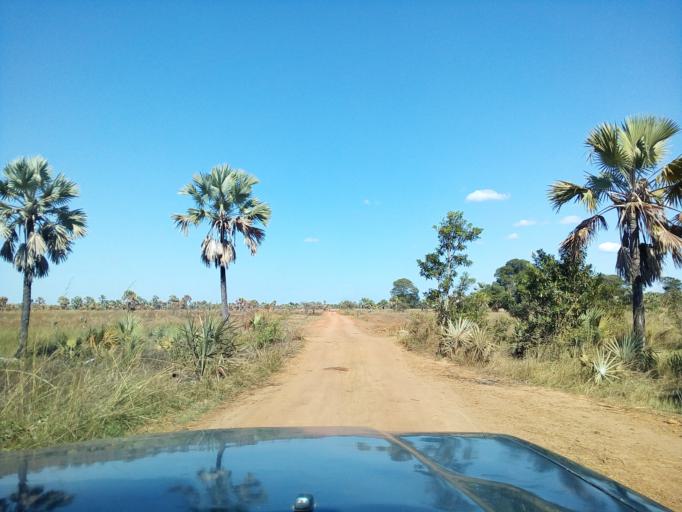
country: MG
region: Boeny
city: Mahajanga
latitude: -15.8569
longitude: 46.1510
